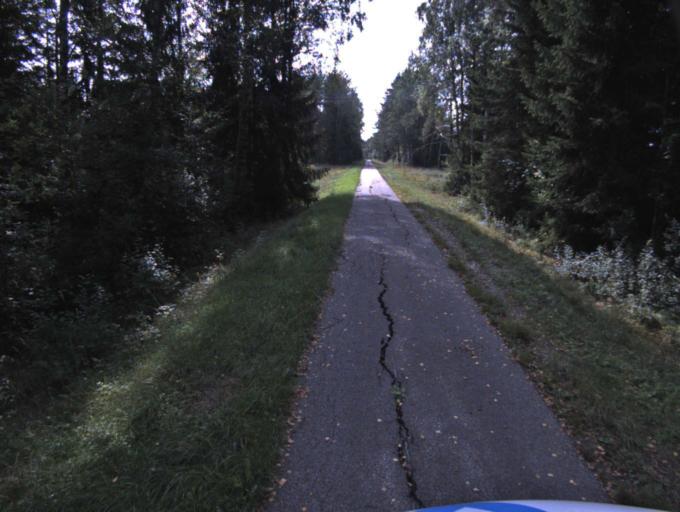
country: SE
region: Vaestra Goetaland
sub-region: Tranemo Kommun
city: Limmared
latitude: 57.6173
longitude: 13.3441
